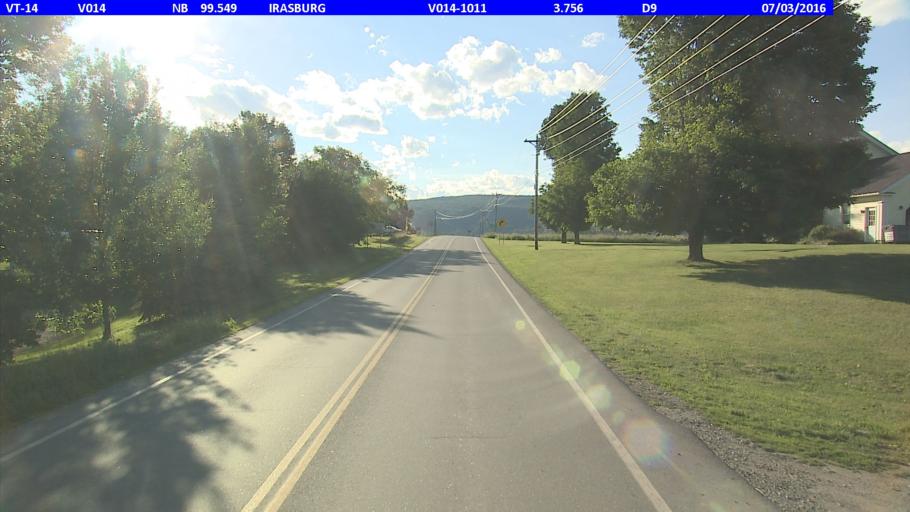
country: US
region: Vermont
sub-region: Orleans County
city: Newport
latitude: 44.8146
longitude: -72.2934
